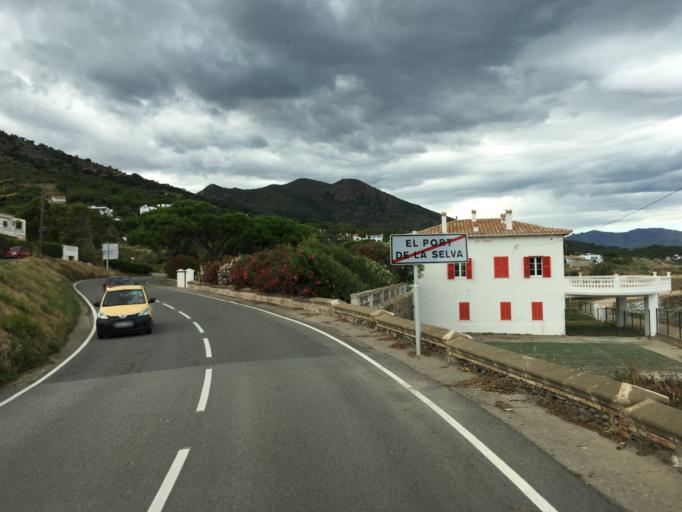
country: ES
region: Catalonia
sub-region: Provincia de Girona
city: Llanca
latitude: 42.3346
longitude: 3.1965
